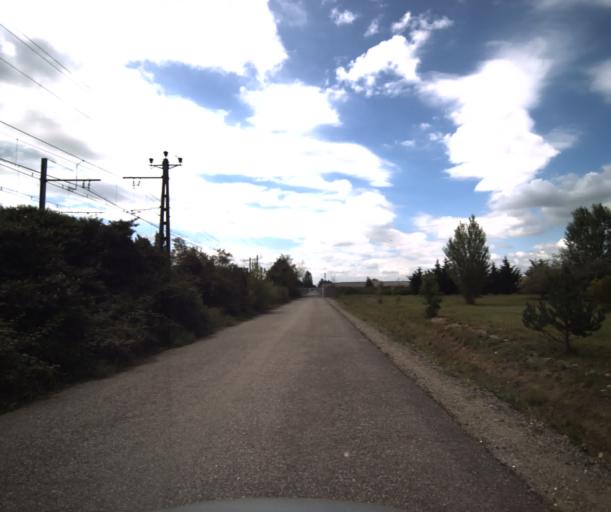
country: FR
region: Midi-Pyrenees
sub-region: Departement de la Haute-Garonne
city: Noe
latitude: 43.3696
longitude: 1.2595
